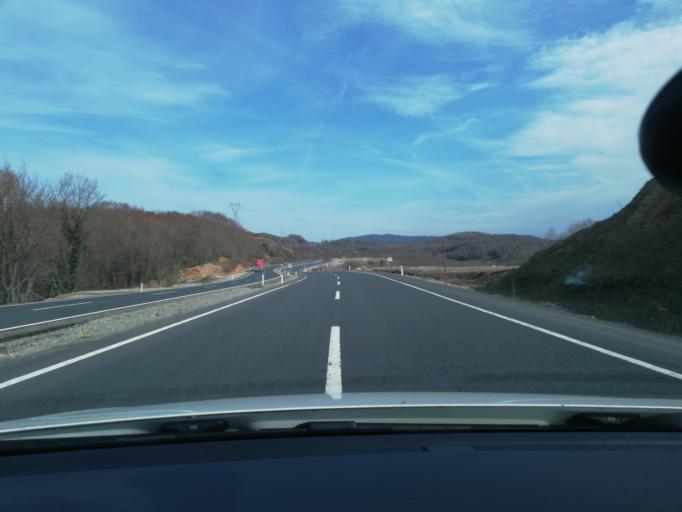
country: TR
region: Zonguldak
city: Eregli
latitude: 41.3312
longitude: 31.5776
